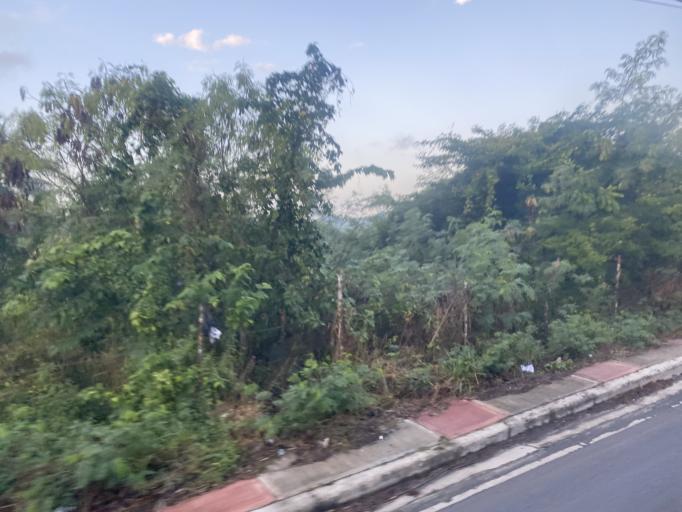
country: DO
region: San Juan
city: Punta Cana
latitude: 18.7122
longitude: -68.4654
